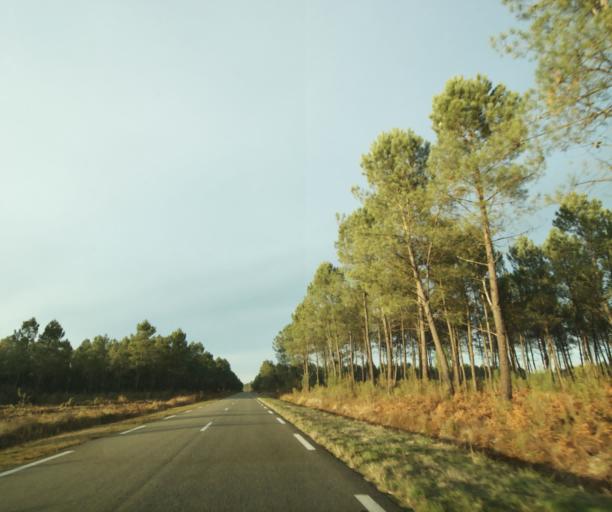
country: FR
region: Aquitaine
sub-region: Departement des Landes
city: Gabarret
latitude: 44.1612
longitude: -0.1340
